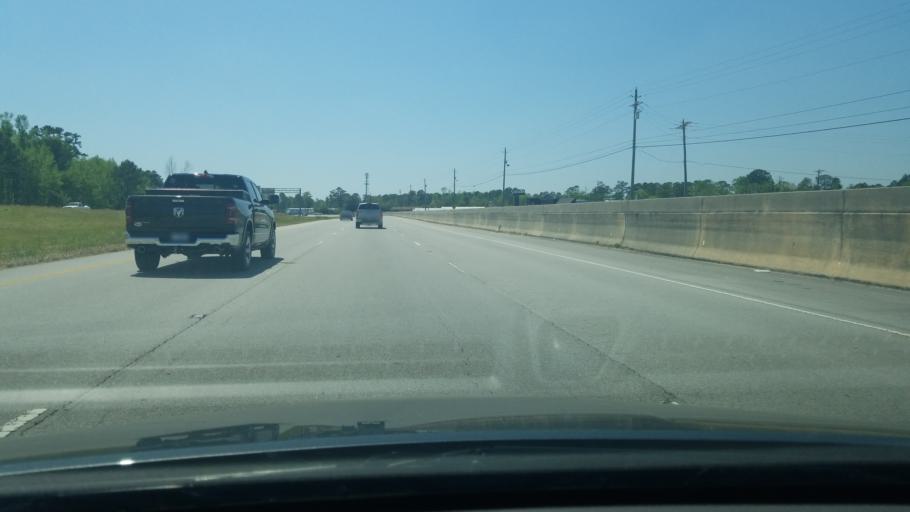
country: US
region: North Carolina
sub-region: Onslow County
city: Jacksonville
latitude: 34.7389
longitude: -77.4636
